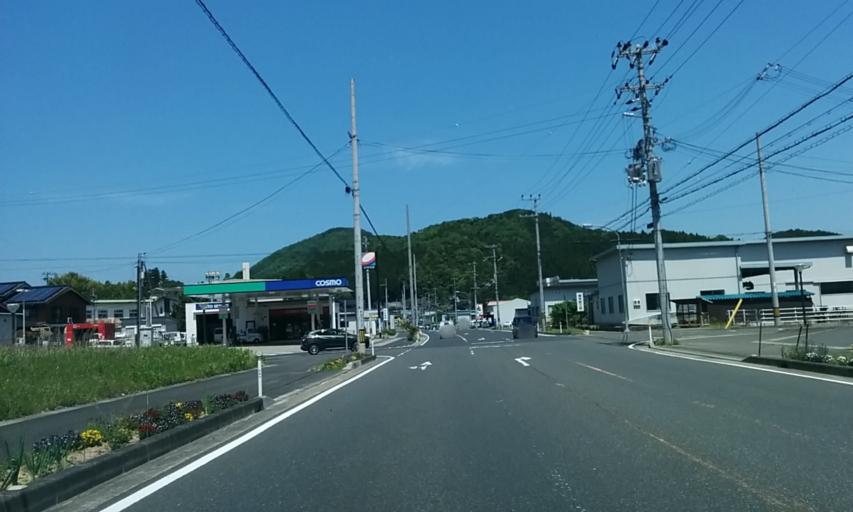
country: JP
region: Kyoto
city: Fukuchiyama
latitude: 35.3913
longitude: 135.1477
